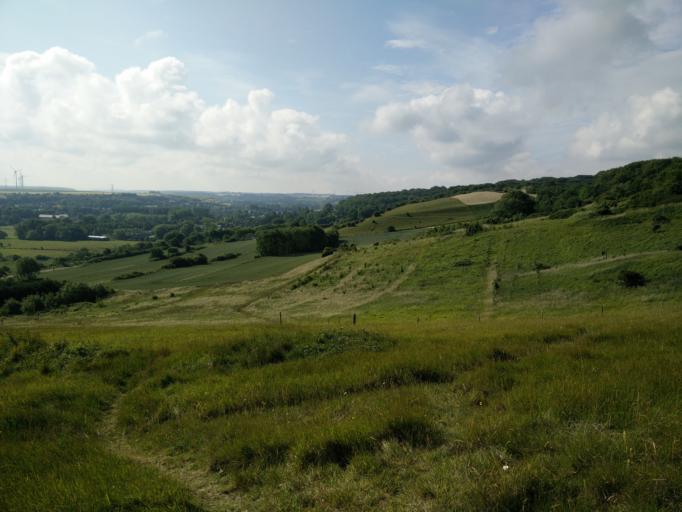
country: FR
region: Haute-Normandie
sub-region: Departement de la Seine-Maritime
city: Criel-sur-Mer
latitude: 50.0306
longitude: 1.3045
